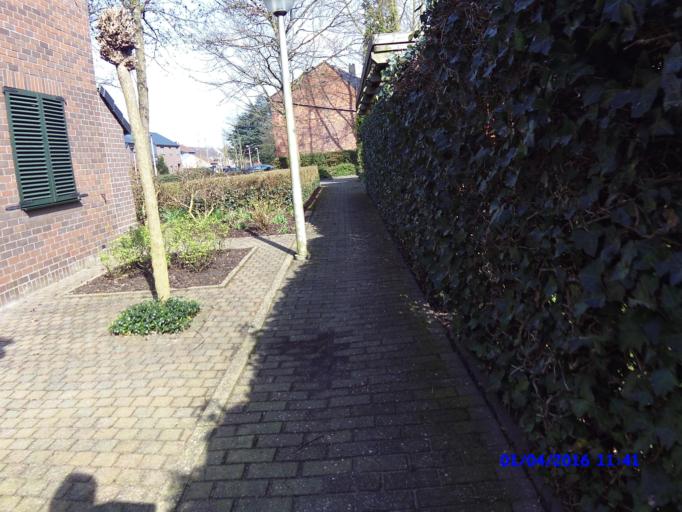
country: BE
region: Flanders
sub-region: Provincie Antwerpen
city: Brasschaat
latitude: 51.2890
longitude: 4.5138
